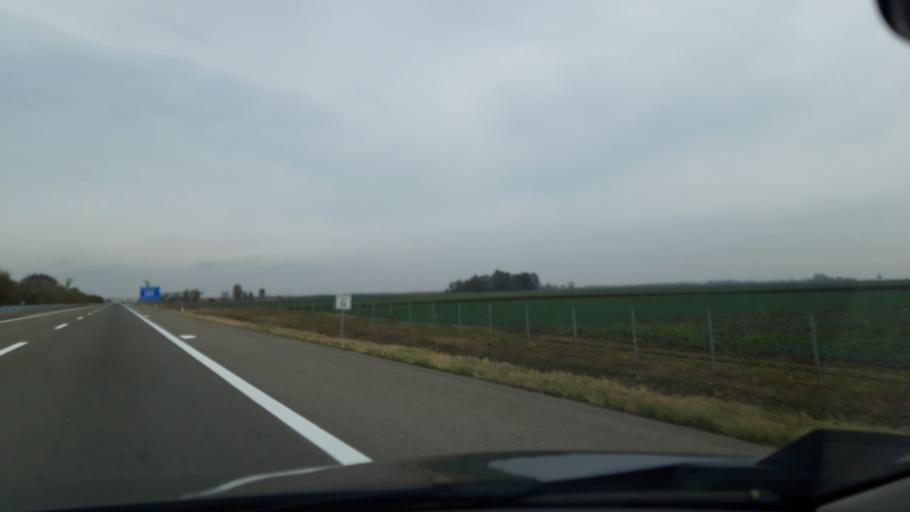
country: RS
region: Autonomna Pokrajina Vojvodina
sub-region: Severnobacki Okrug
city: Backa Topola
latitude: 45.7894
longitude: 19.6956
